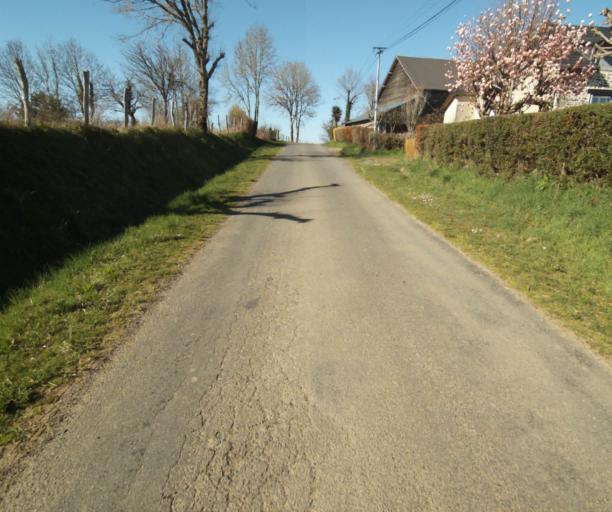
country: FR
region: Limousin
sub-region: Departement de la Correze
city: Chamboulive
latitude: 45.4275
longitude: 1.6512
